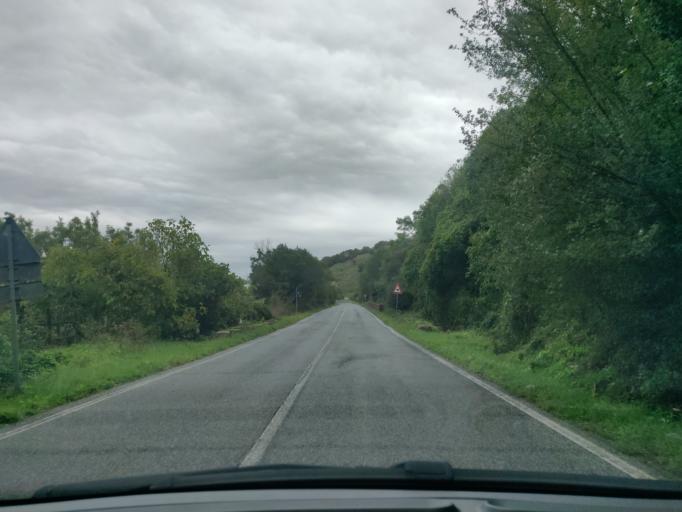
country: IT
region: Latium
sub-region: Citta metropolitana di Roma Capitale
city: Allumiere
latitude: 42.1414
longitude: 11.8776
